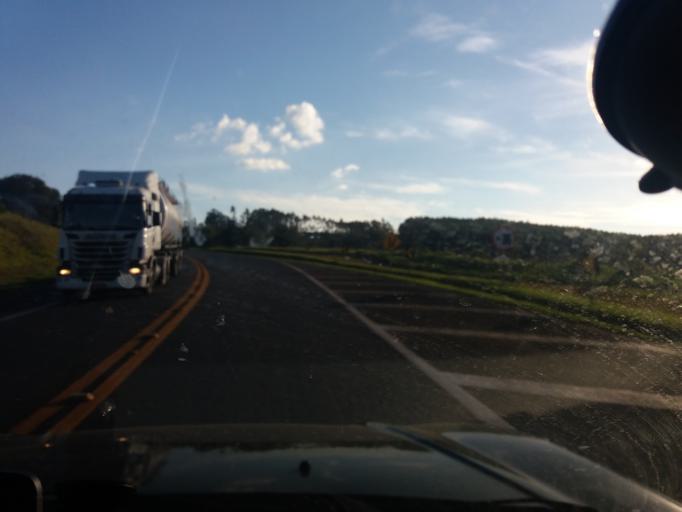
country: BR
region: Sao Paulo
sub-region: Buri
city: Buri
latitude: -23.9274
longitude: -48.6622
